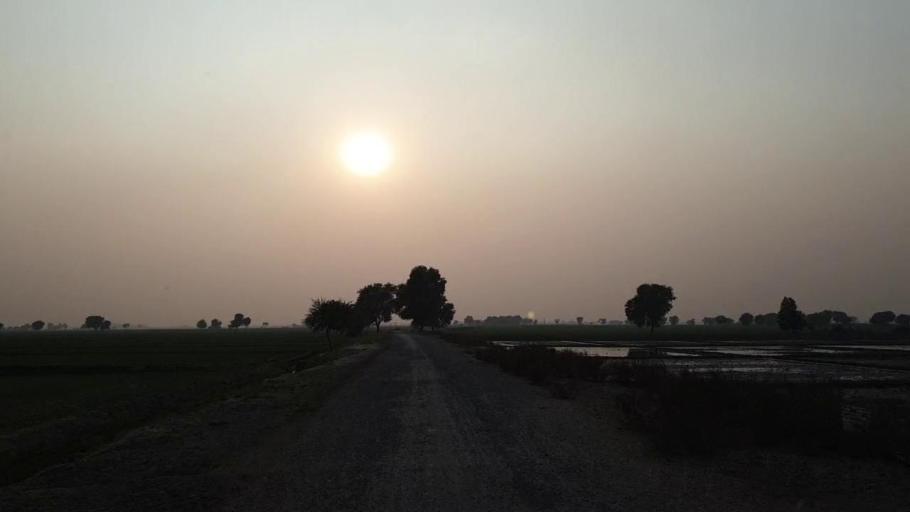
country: PK
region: Sindh
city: Bhan
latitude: 26.5082
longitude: 67.7199
